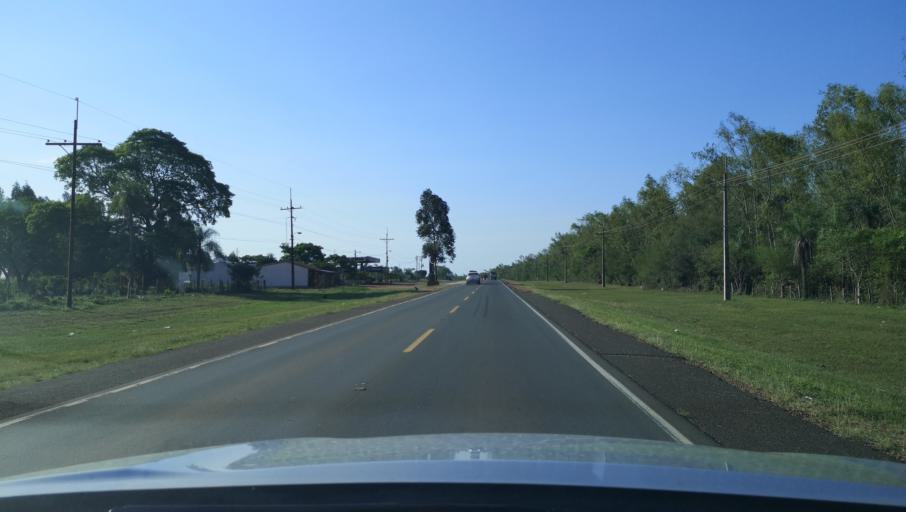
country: PY
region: Misiones
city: Santa Maria
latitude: -26.7652
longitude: -57.0324
